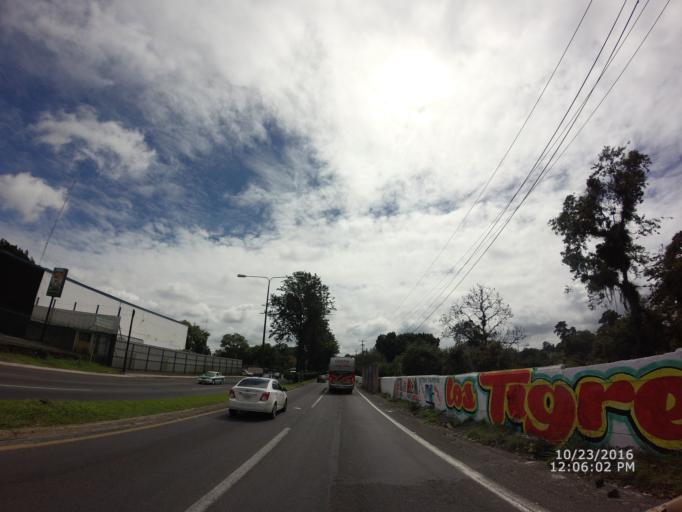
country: MX
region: Veracruz
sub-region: Xalapa
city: Lomas Verdes
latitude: 19.5236
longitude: -96.8959
